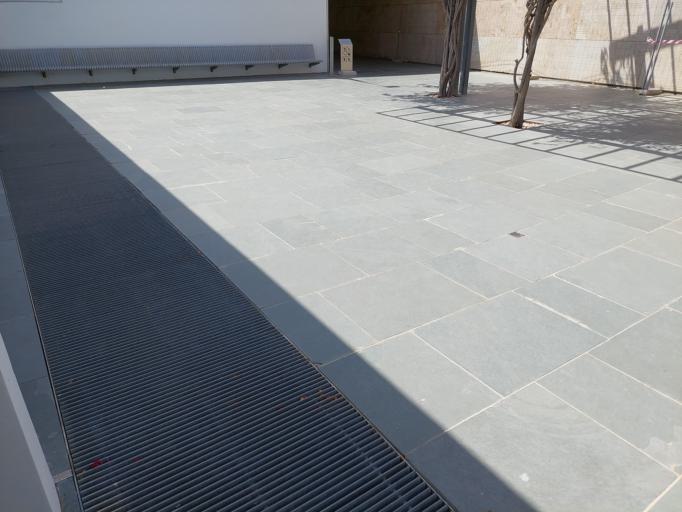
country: ES
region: Andalusia
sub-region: Provincia de Cadiz
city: Zahara de los Atunes
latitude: 36.0899
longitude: -5.7713
